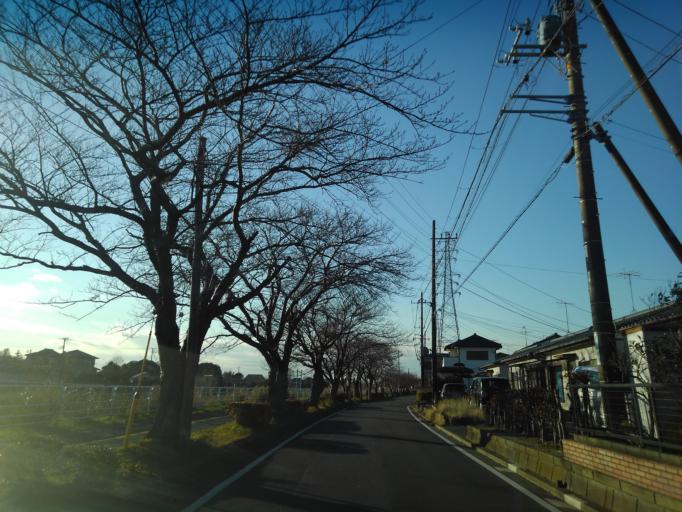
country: JP
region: Chiba
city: Kimitsu
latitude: 35.3238
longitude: 139.9001
